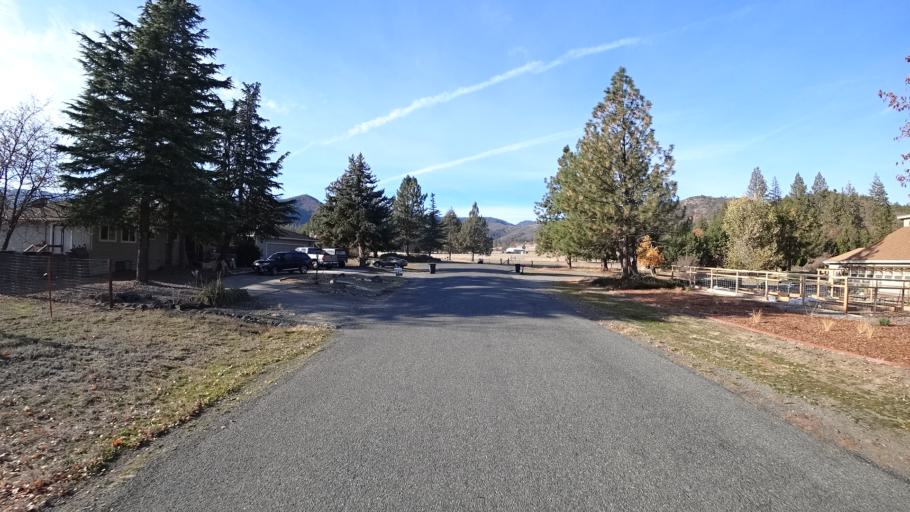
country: US
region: California
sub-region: Siskiyou County
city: Yreka
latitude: 41.6823
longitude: -122.6380
